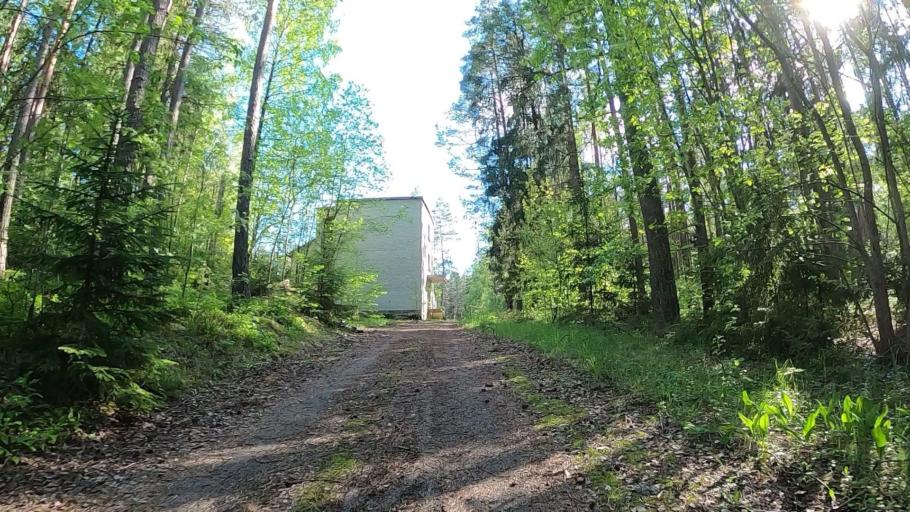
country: LV
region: Baldone
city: Baldone
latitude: 56.7756
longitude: 24.4101
